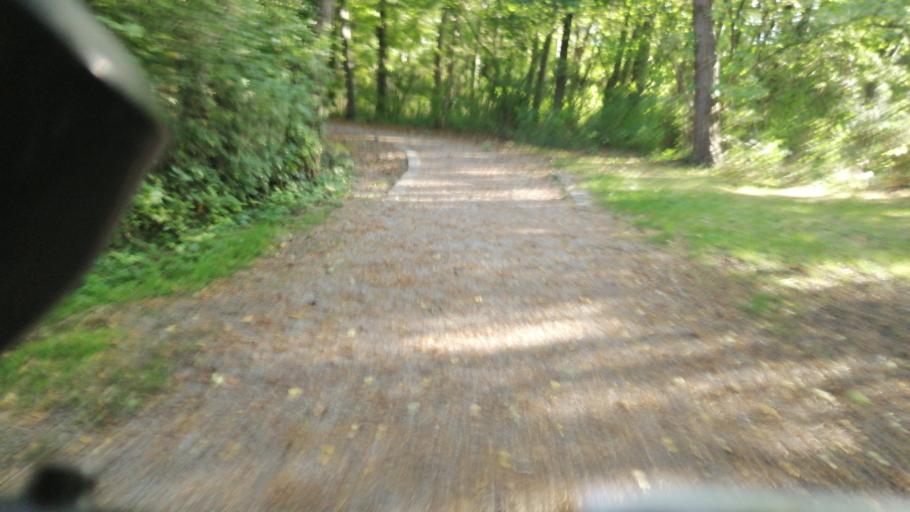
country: DE
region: Bavaria
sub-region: Upper Bavaria
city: Unterfoehring
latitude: 48.2063
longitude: 11.6038
